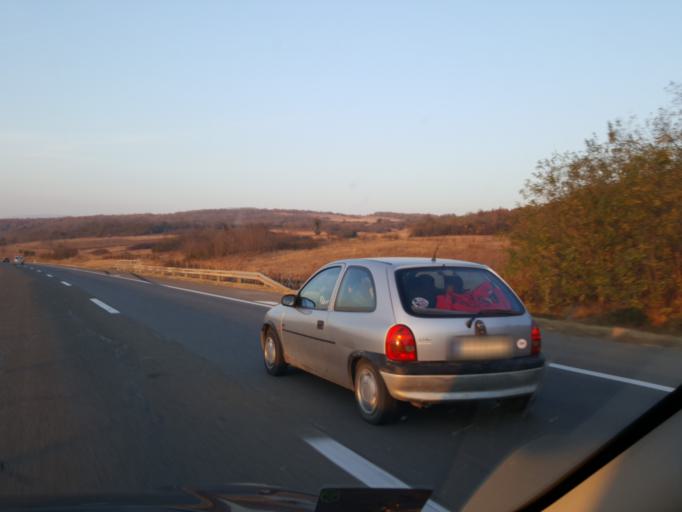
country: RS
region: Central Serbia
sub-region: Nisavski Okrug
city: Aleksinac
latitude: 43.4331
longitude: 21.8001
